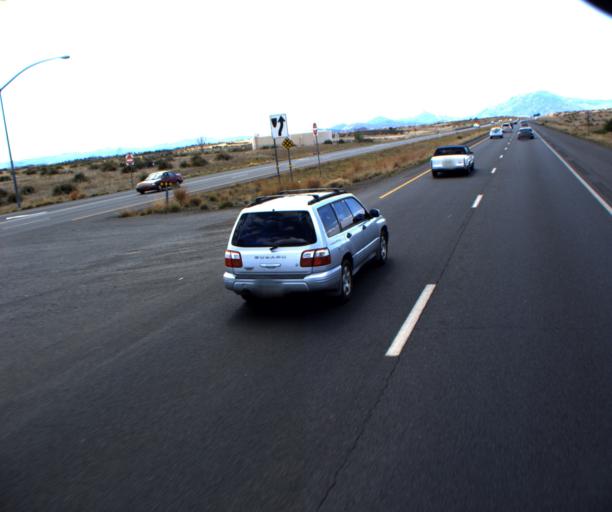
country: US
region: Arizona
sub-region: Yavapai County
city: Prescott Valley
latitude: 34.6307
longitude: -112.3752
